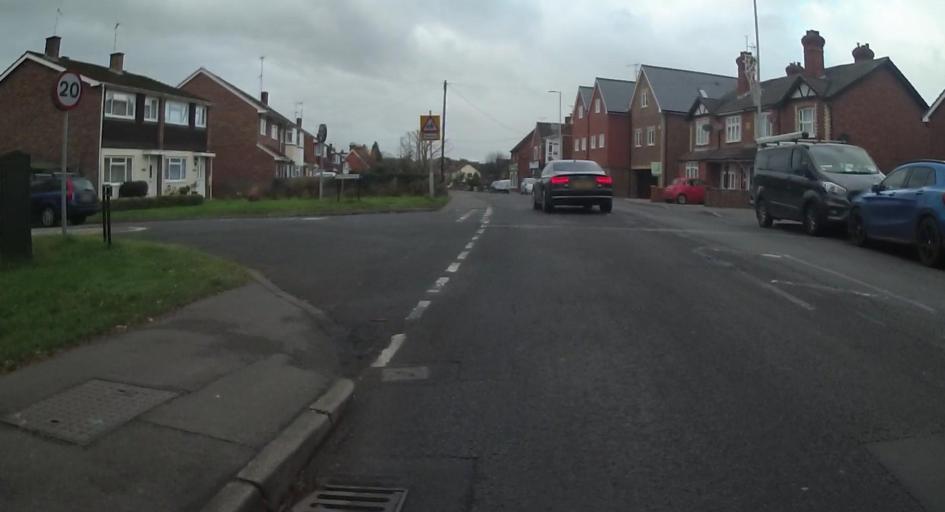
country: GB
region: England
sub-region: Bracknell Forest
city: Sandhurst
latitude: 51.3418
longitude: -0.7789
